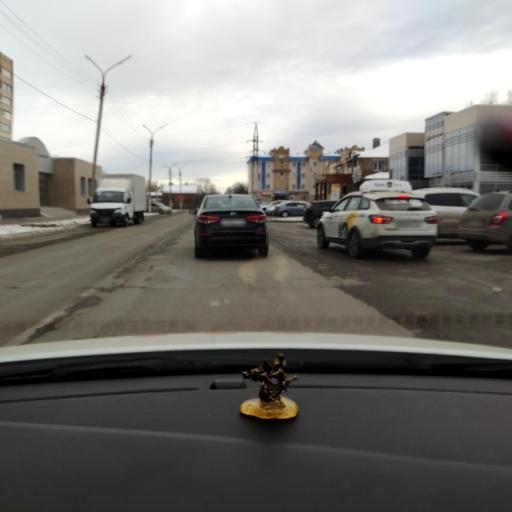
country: RU
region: Tatarstan
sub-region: Zelenodol'skiy Rayon
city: Zelenodolsk
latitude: 55.8452
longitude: 48.5251
